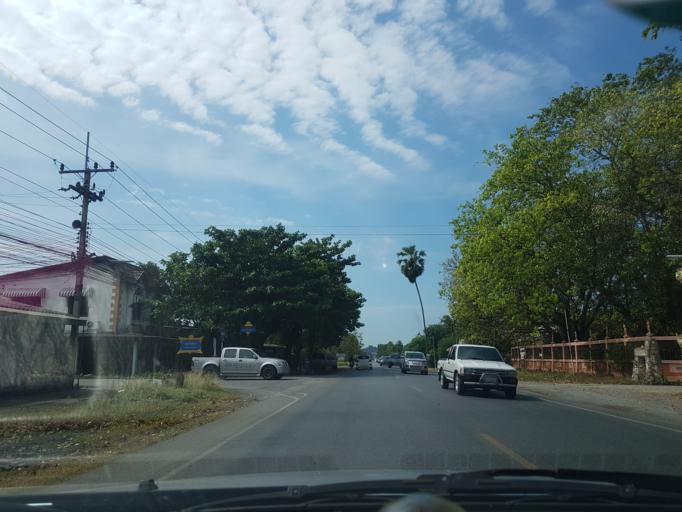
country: TH
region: Lop Buri
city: Lop Buri
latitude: 14.8009
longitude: 100.7361
